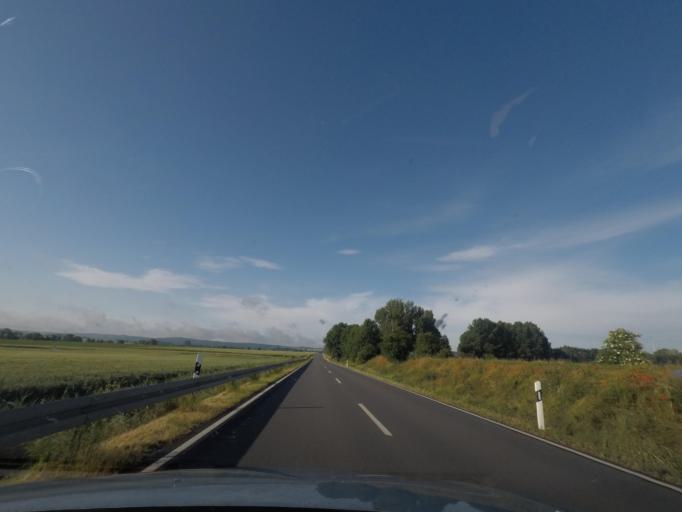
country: DE
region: Saxony-Anhalt
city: Huy-Neinstedt
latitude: 52.0043
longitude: 10.8951
